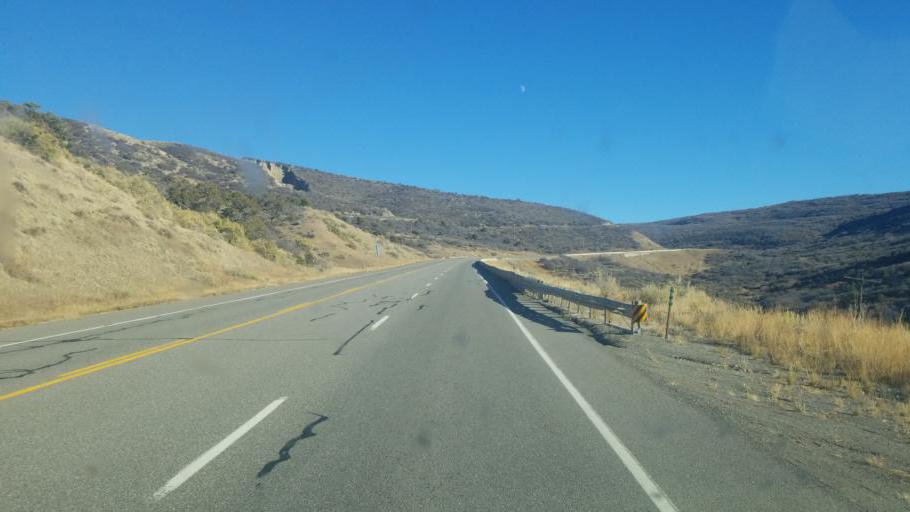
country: US
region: Colorado
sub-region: Montrose County
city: Montrose
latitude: 38.4579
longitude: -107.6674
